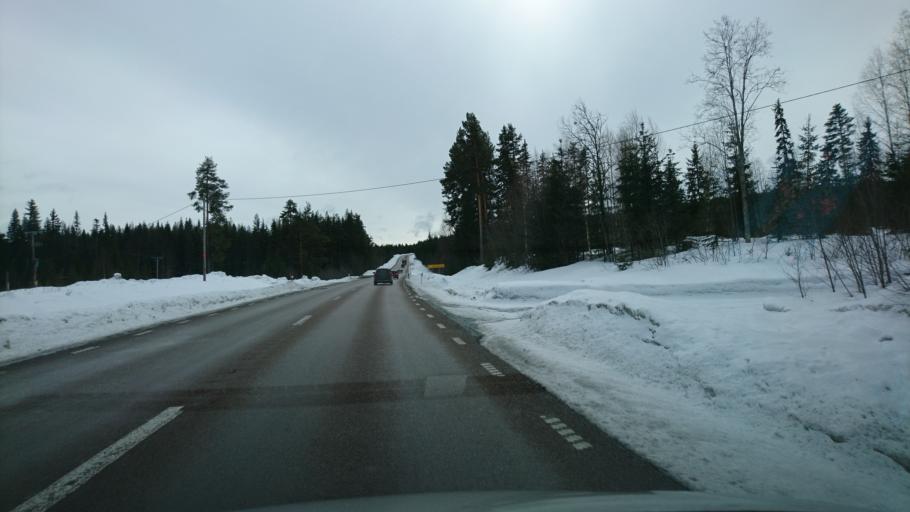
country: SE
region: Vaesternorrland
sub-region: Solleftea Kommun
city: Solleftea
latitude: 63.0929
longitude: 17.0167
